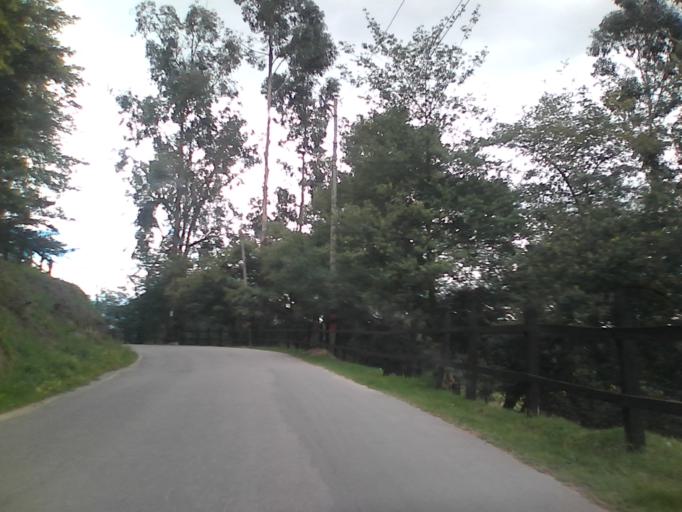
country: CO
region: Boyaca
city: Duitama
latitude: 5.8050
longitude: -73.0629
